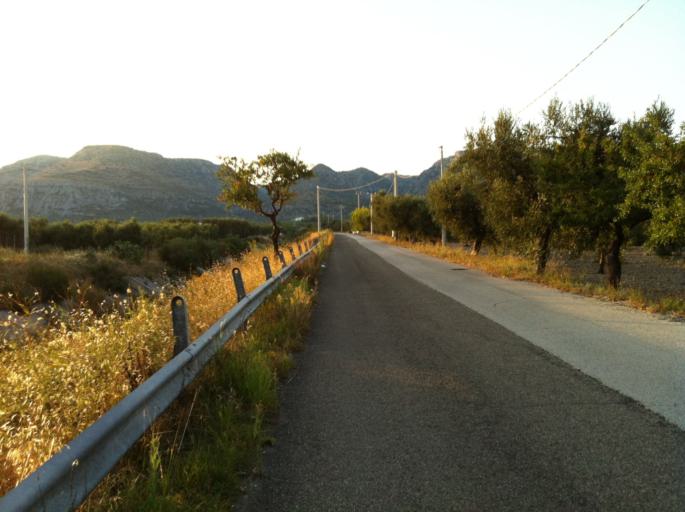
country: IT
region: Apulia
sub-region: Provincia di Foggia
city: Monte Sant'Angelo
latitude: 41.6581
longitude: 15.9509
